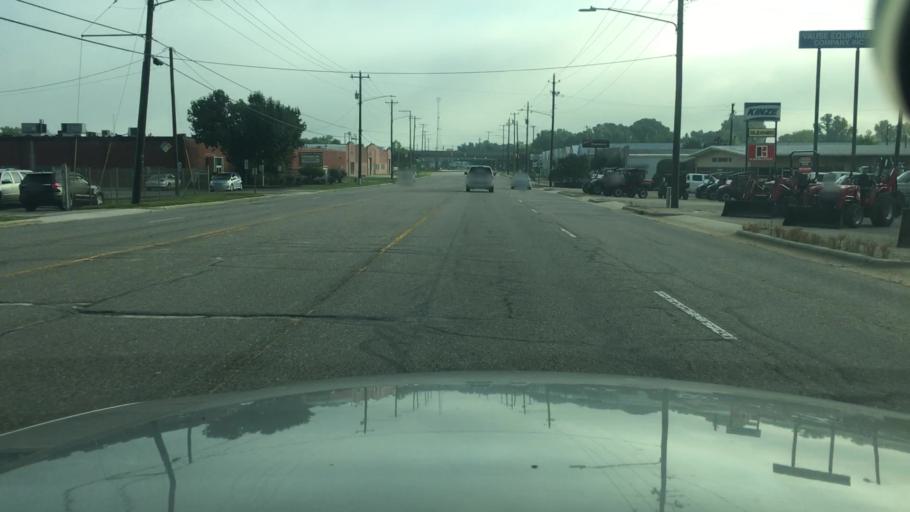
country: US
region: North Carolina
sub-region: Cumberland County
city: Fayetteville
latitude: 35.0343
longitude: -78.8853
